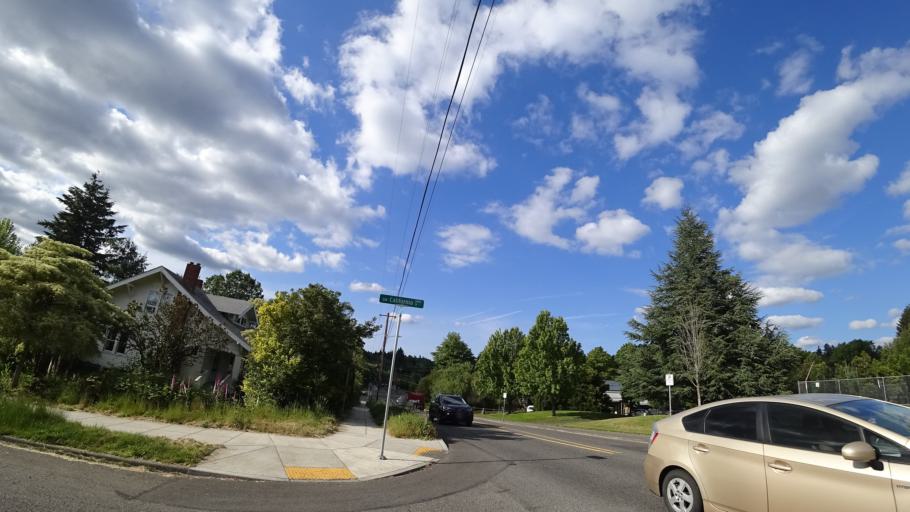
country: US
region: Oregon
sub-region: Washington County
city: Garden Home-Whitford
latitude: 45.4749
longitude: -122.7233
